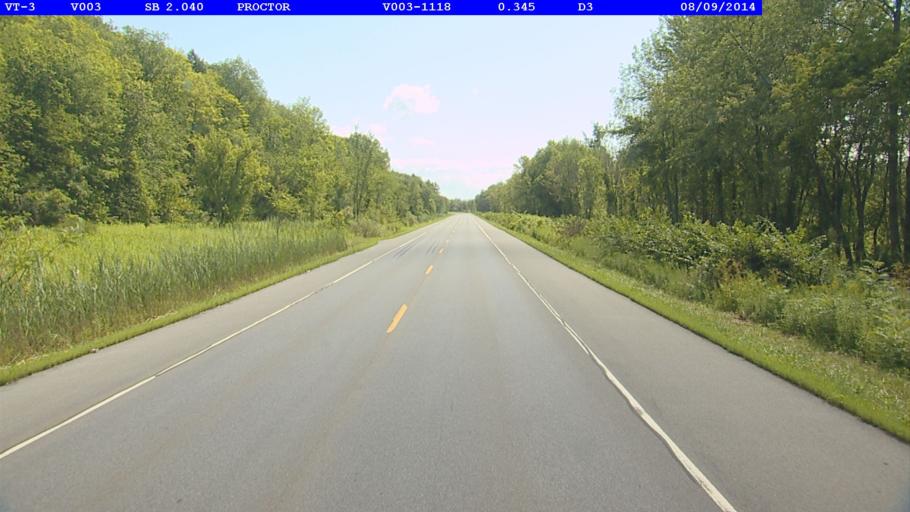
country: US
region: Vermont
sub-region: Rutland County
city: West Rutland
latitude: 43.6294
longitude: -73.0324
